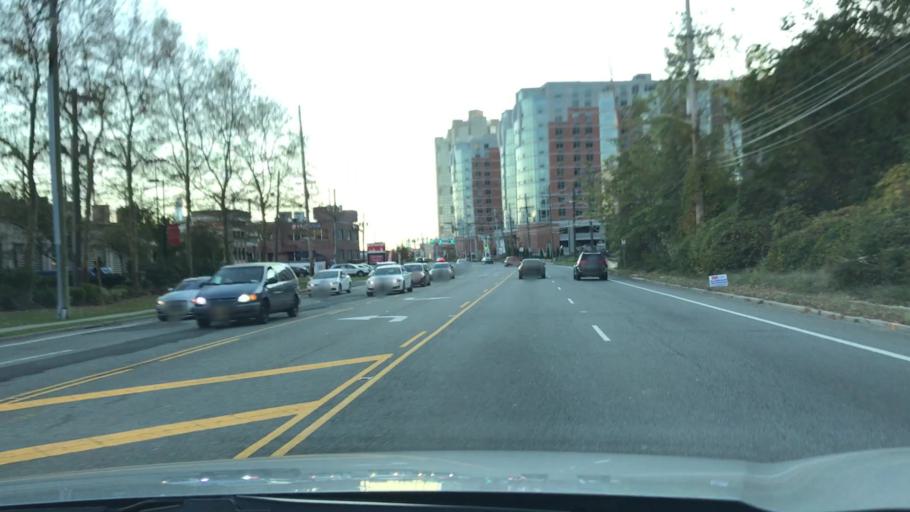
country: US
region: New Jersey
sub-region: Hudson County
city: Guttenberg
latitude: 40.7974
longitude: -73.9960
